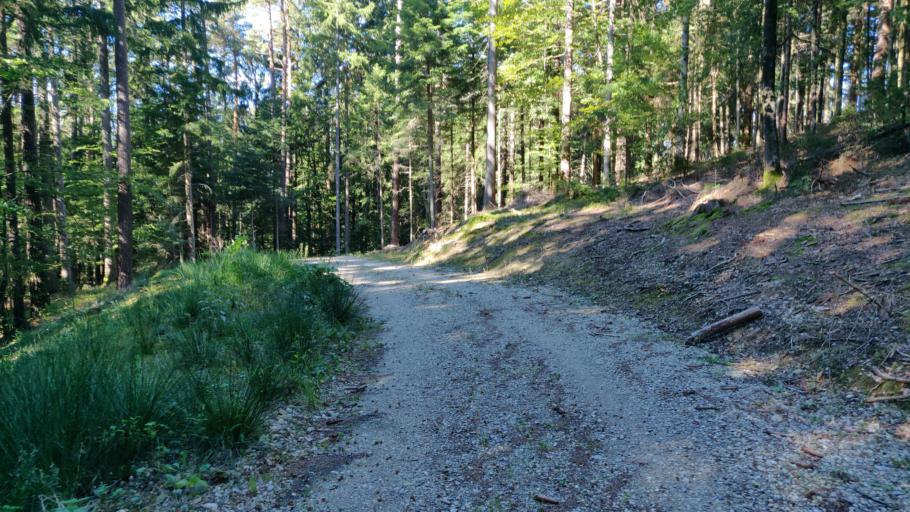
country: CH
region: Bern
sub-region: Oberaargau
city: Rohrbach
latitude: 47.1304
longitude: 7.7905
